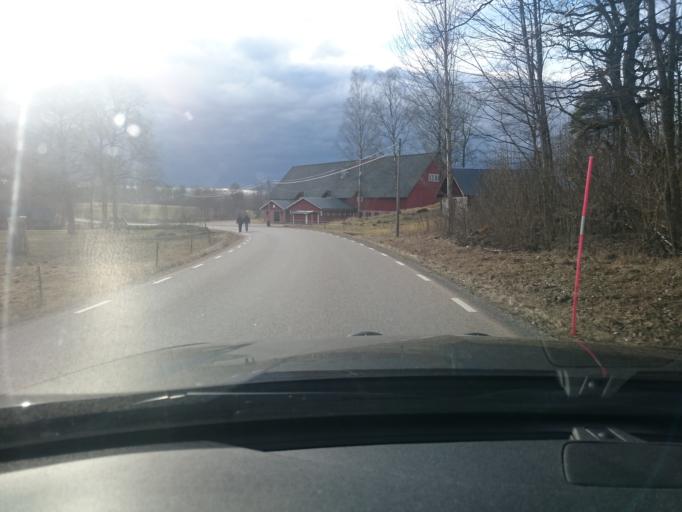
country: SE
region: Joenkoeping
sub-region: Vetlanda Kommun
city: Vetlanda
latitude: 57.3179
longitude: 15.1305
